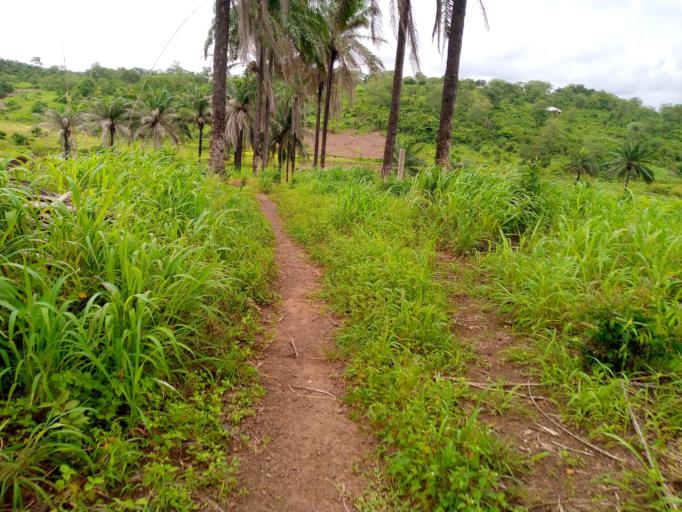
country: SL
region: Southern Province
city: Moyamba
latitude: 8.1534
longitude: -12.4440
